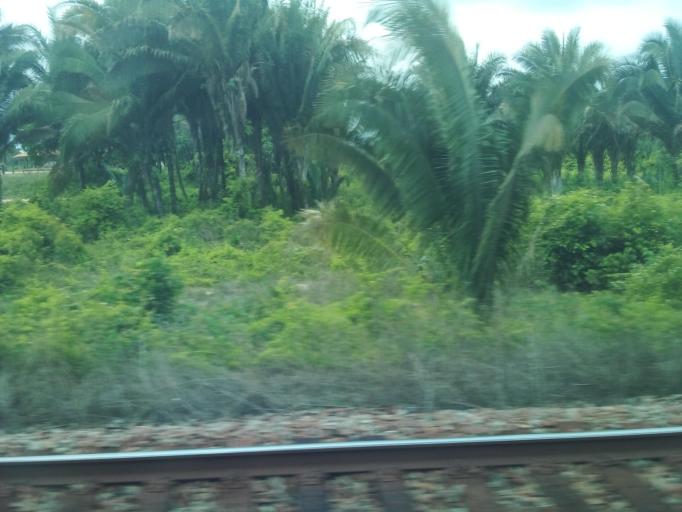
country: BR
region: Maranhao
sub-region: Santa Ines
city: Santa Ines
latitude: -3.6525
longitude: -45.8055
